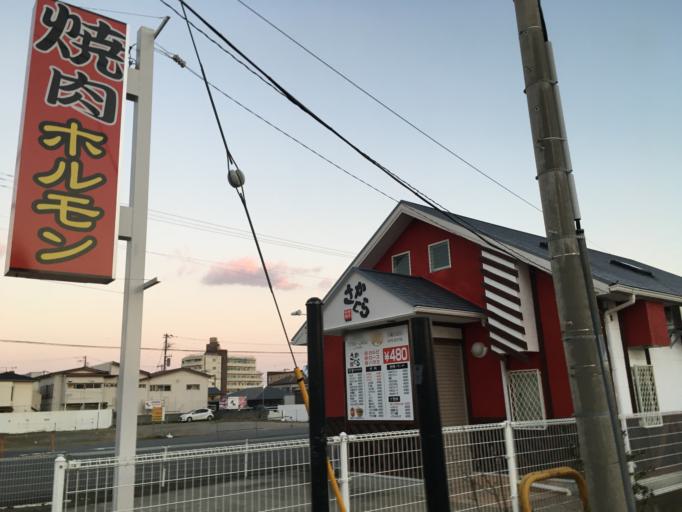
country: JP
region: Chiba
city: Tateyama
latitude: 34.9934
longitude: 139.8612
